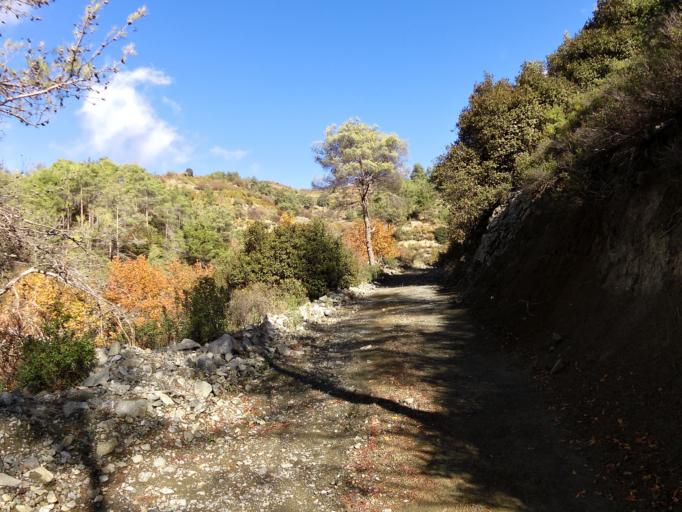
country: CY
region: Limassol
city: Kyperounta
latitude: 34.9285
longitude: 32.9456
